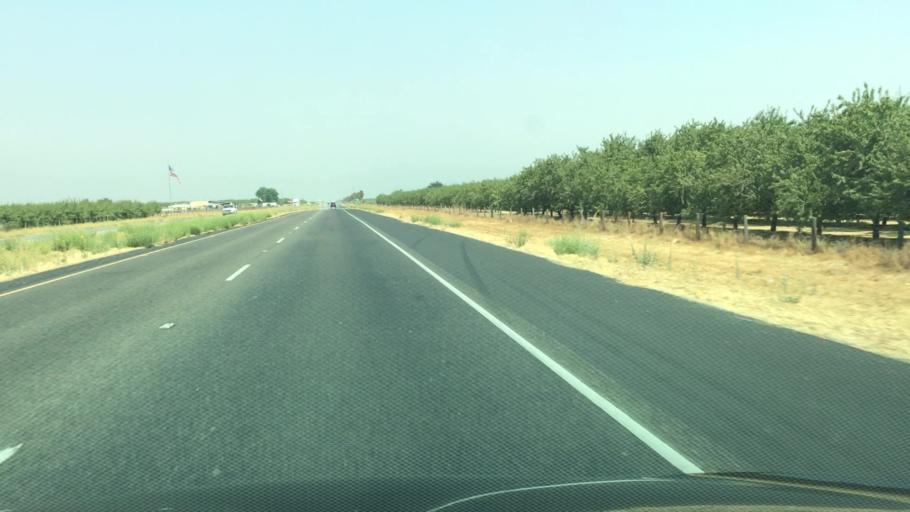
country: US
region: California
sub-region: Madera County
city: Chowchilla
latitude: 37.0834
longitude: -120.4257
